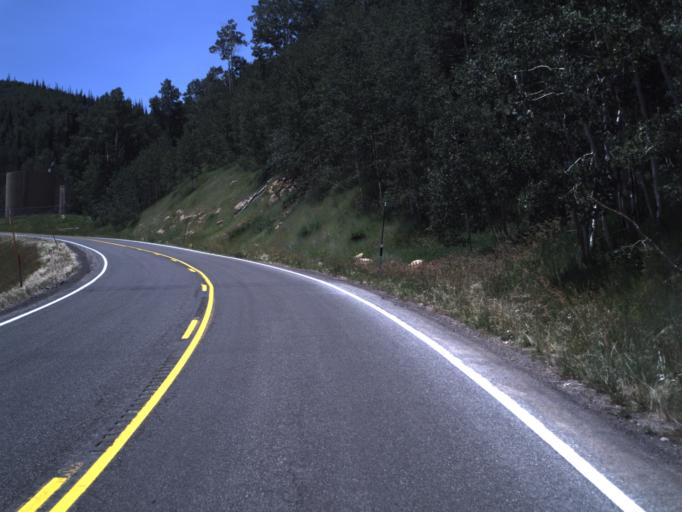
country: US
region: Utah
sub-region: Sanpete County
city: Fairview
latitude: 39.6807
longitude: -111.2108
